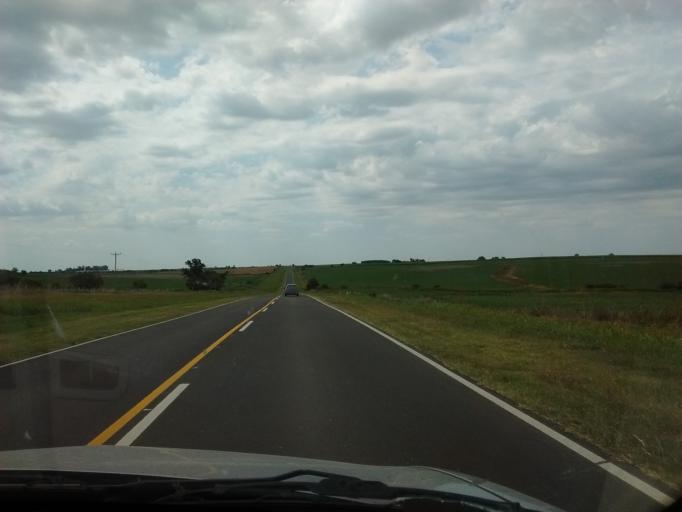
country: AR
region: Entre Rios
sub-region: Departamento de Victoria
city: Victoria
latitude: -32.8243
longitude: -59.8770
